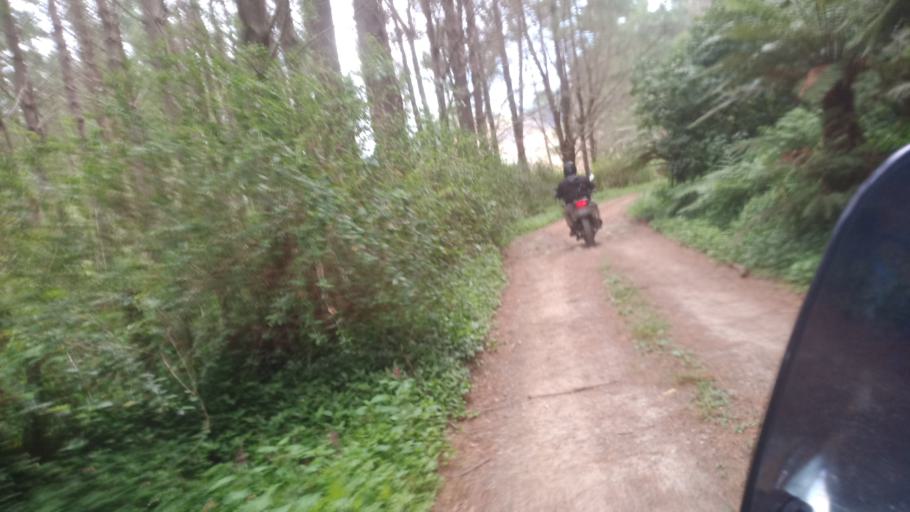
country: NZ
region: Gisborne
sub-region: Gisborne District
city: Gisborne
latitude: -38.4606
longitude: 177.9089
